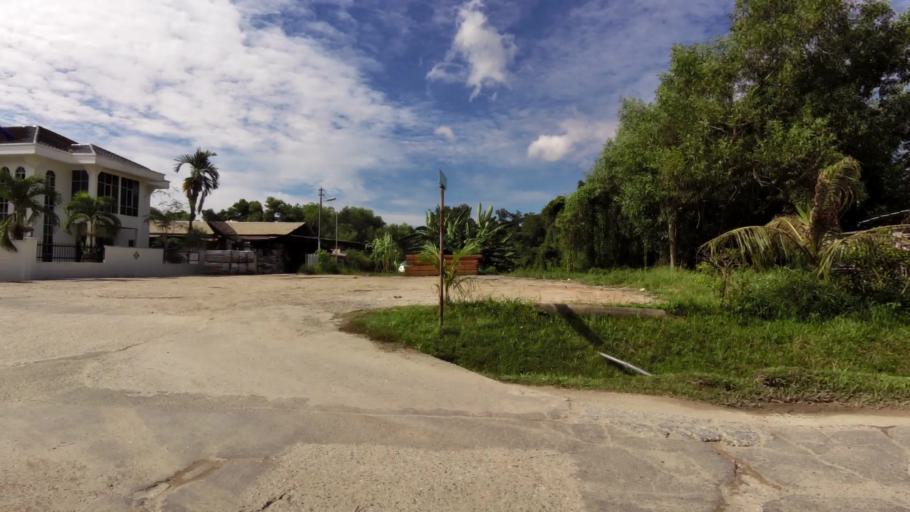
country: BN
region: Brunei and Muara
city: Bandar Seri Begawan
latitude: 4.9253
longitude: 114.9075
